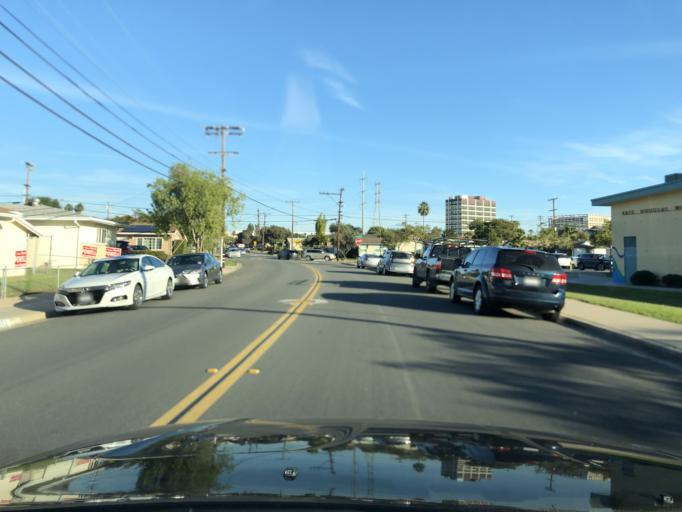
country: US
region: California
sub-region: San Diego County
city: La Jolla
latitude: 32.8210
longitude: -117.1871
